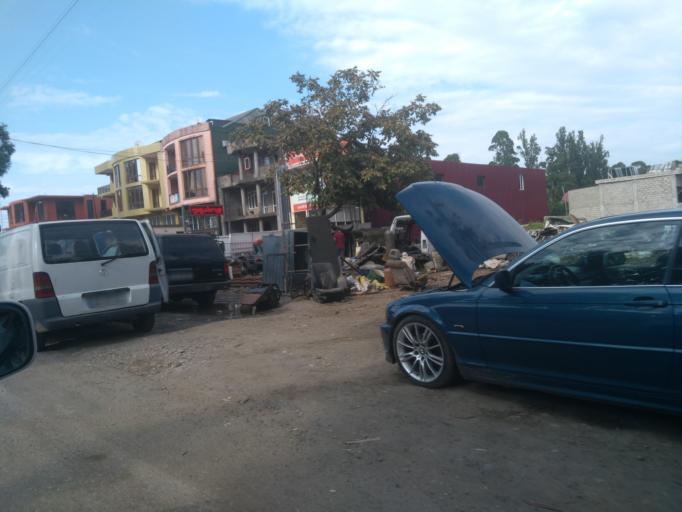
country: GE
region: Ajaria
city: Batumi
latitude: 41.6080
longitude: 41.6272
